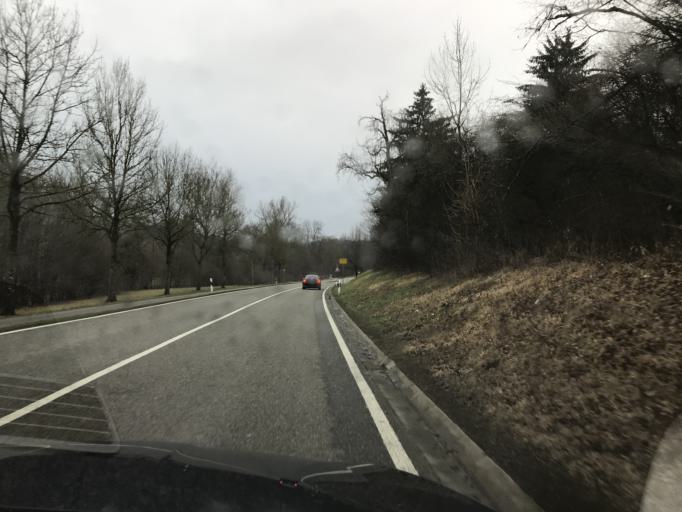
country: DE
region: Baden-Wuerttemberg
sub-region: Regierungsbezirk Stuttgart
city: Wolfschlugen
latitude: 48.6299
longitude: 9.2769
